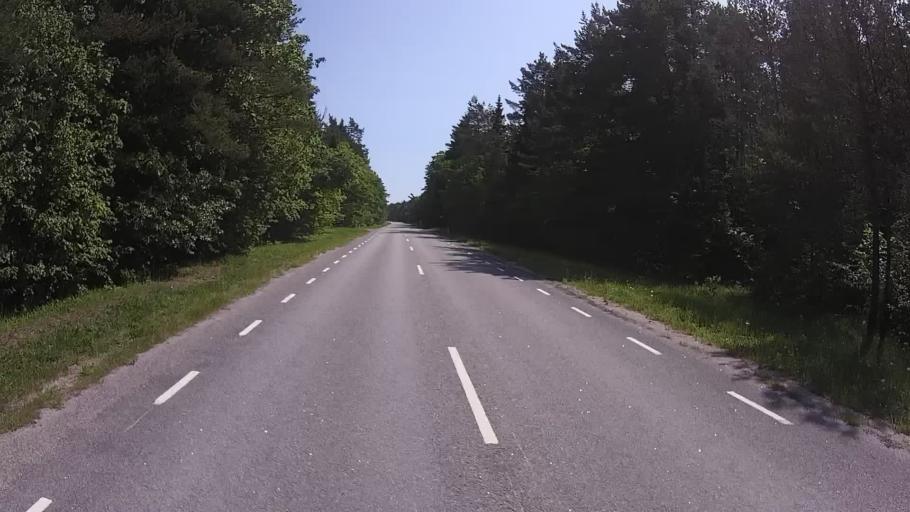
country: EE
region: Saare
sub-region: Kuressaare linn
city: Kuressaare
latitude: 58.3572
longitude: 22.0663
